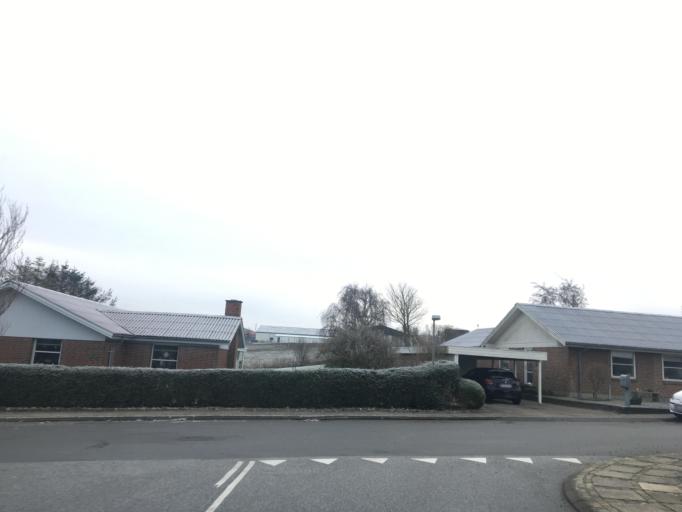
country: DK
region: North Denmark
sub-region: Thisted Kommune
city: Hurup
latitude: 56.7531
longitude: 8.4309
